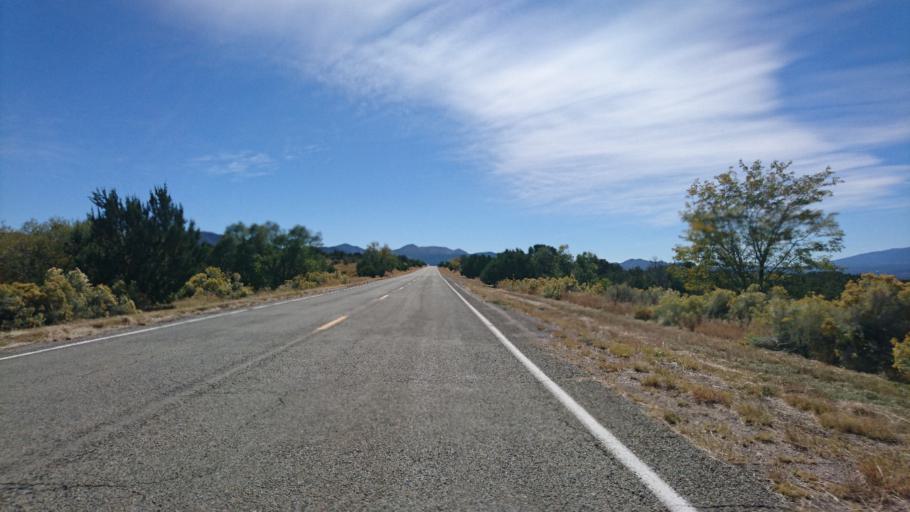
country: US
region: New Mexico
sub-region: Bernalillo County
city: Sandia Knolls
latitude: 35.3110
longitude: -106.2153
